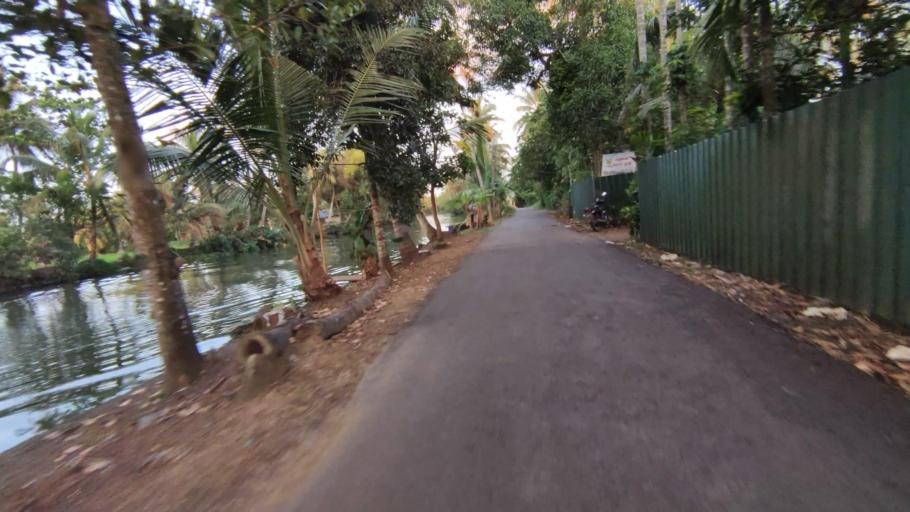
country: IN
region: Kerala
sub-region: Kottayam
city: Kottayam
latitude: 9.5759
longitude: 76.4486
